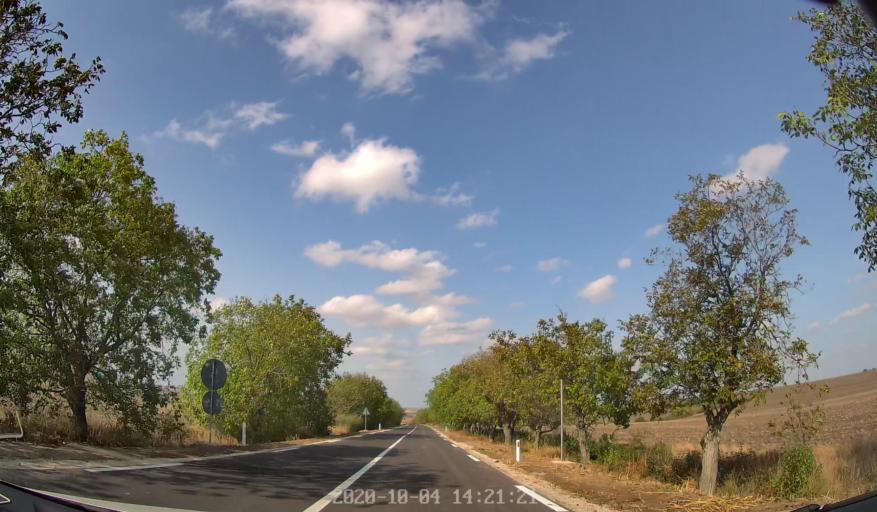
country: MD
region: Rezina
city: Saharna
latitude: 47.5840
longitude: 28.9560
